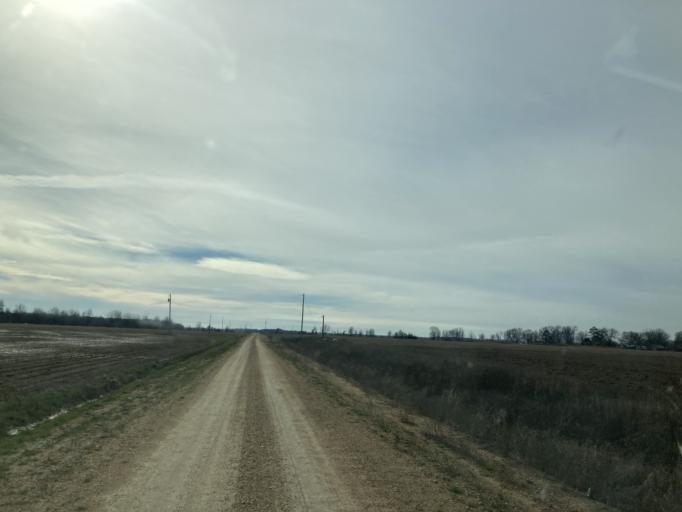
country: US
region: Mississippi
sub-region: Humphreys County
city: Belzoni
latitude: 33.0650
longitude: -90.6576
